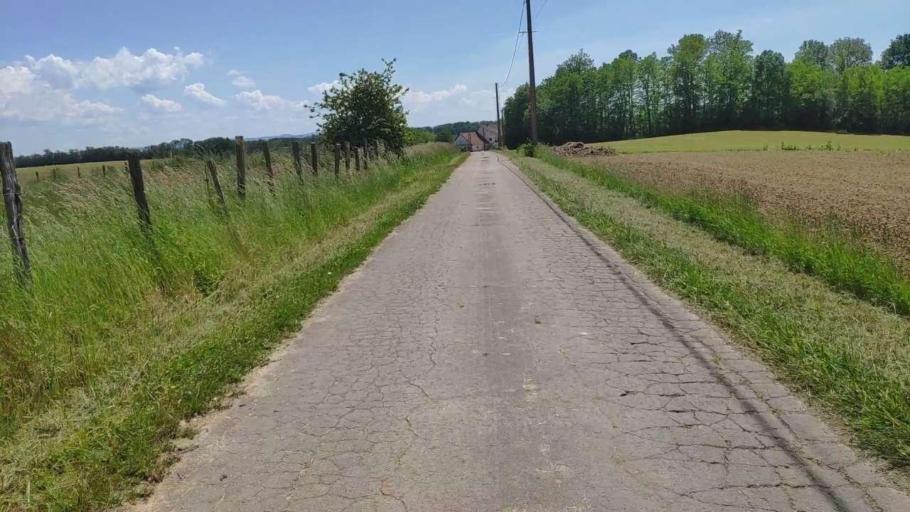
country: FR
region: Franche-Comte
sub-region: Departement du Jura
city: Bletterans
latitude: 46.7601
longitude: 5.4122
